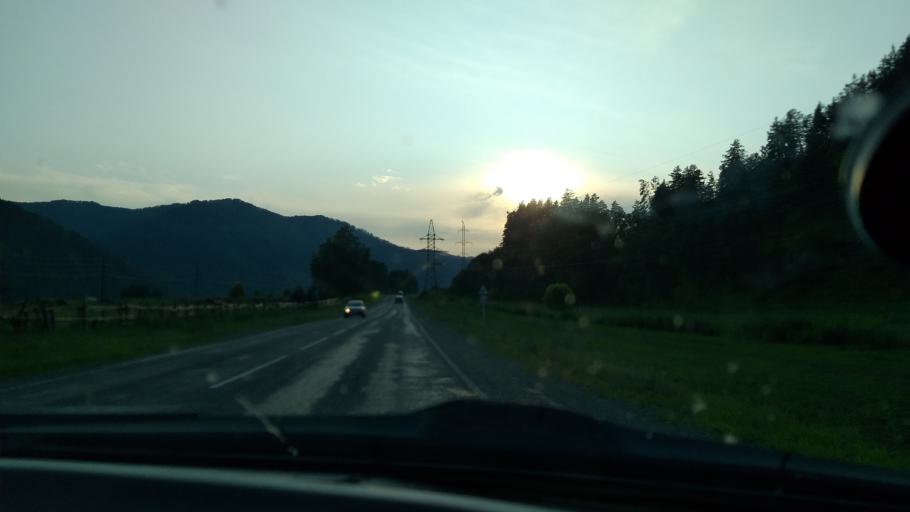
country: RU
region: Altay
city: Elekmonar
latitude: 51.5706
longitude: 85.8816
